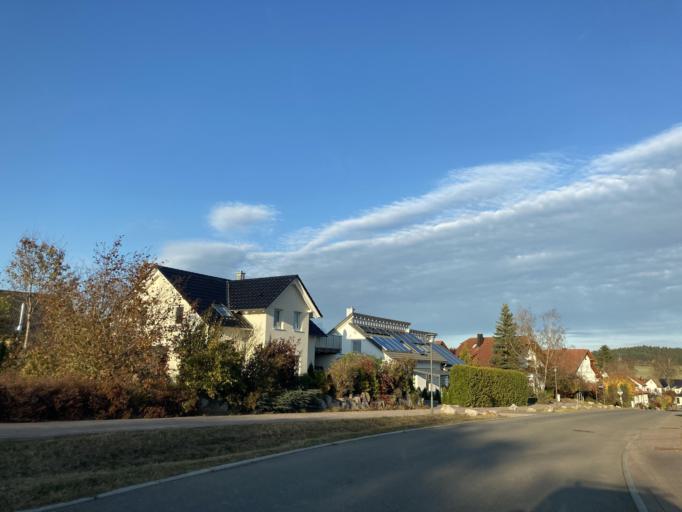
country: DE
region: Baden-Wuerttemberg
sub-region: Freiburg Region
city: Braunlingen
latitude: 47.9966
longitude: 8.4044
